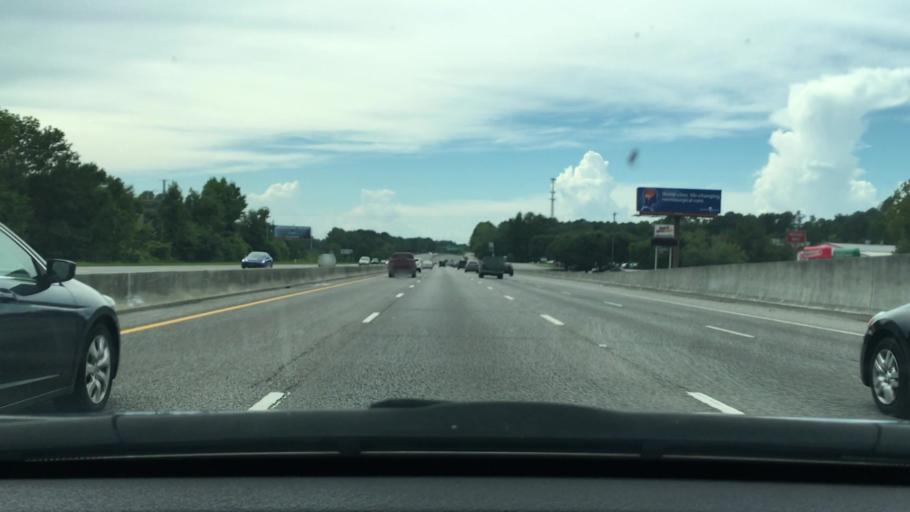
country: US
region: South Carolina
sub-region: Lexington County
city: West Columbia
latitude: 34.0150
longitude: -81.0834
